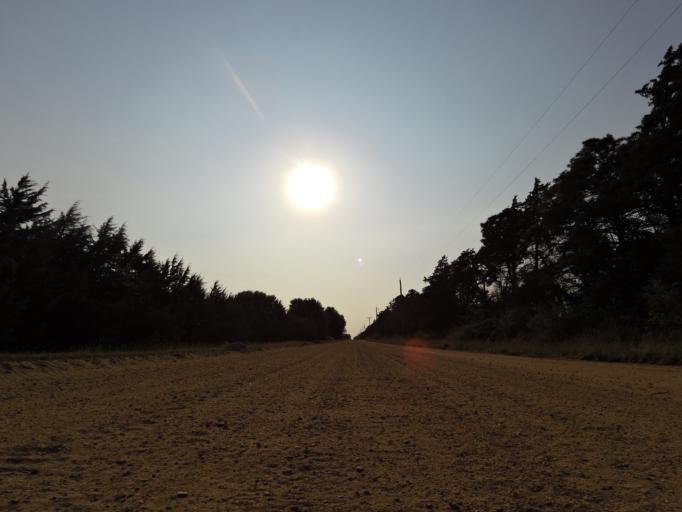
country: US
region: Kansas
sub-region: Reno County
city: South Hutchinson
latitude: 37.9992
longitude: -98.0398
